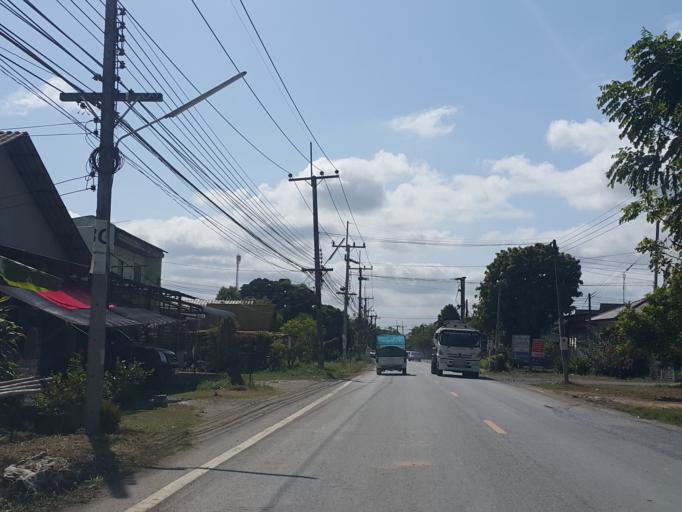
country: TH
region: Chiang Mai
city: San Kamphaeng
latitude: 18.6972
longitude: 99.1605
